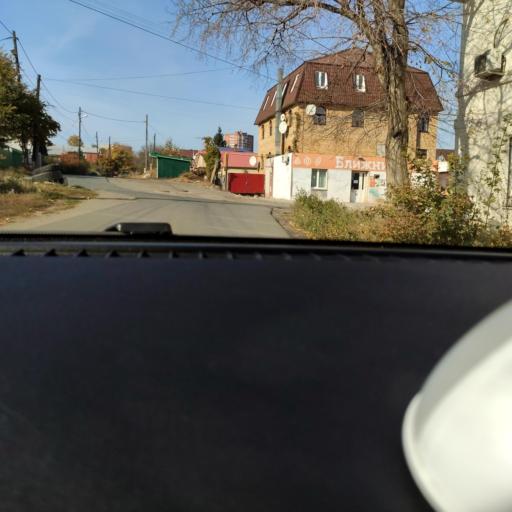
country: RU
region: Samara
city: Samara
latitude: 53.1832
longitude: 50.2055
